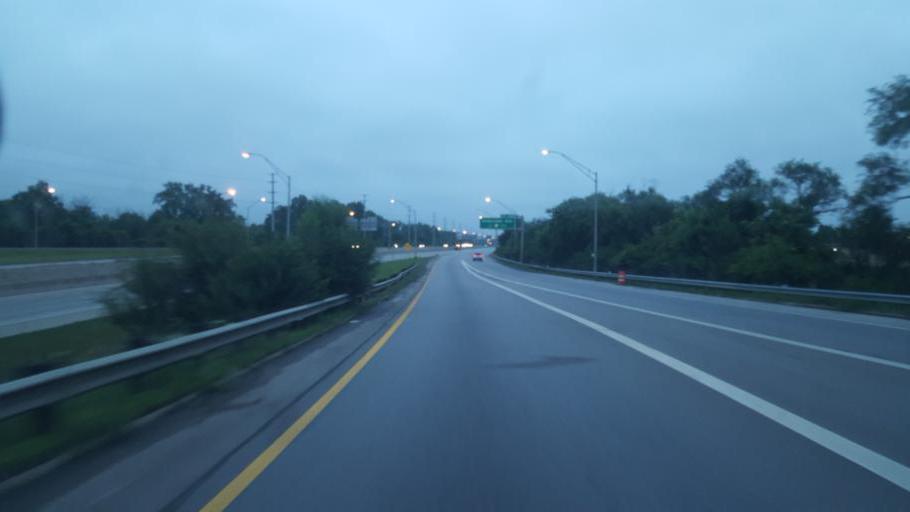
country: US
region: Ohio
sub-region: Franklin County
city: Columbus
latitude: 39.9482
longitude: -83.0160
